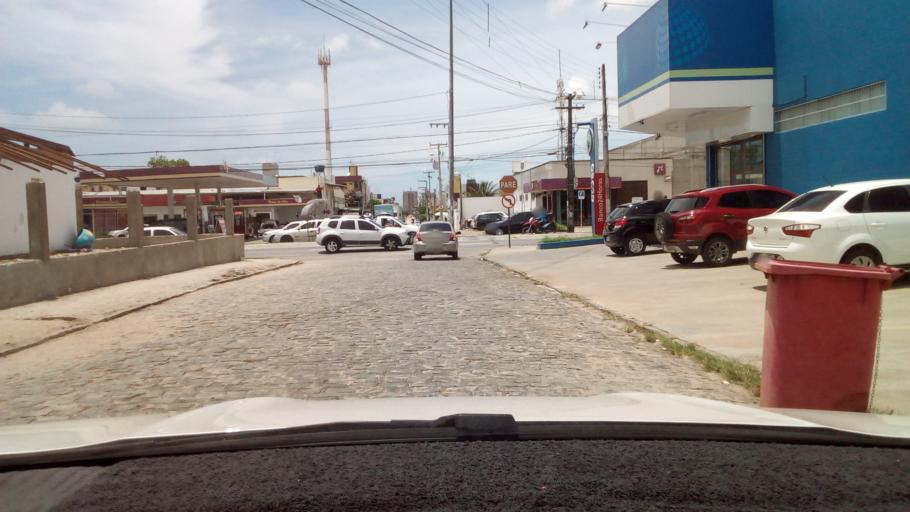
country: BR
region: Paraiba
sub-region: Joao Pessoa
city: Joao Pessoa
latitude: -7.1554
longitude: -34.8393
